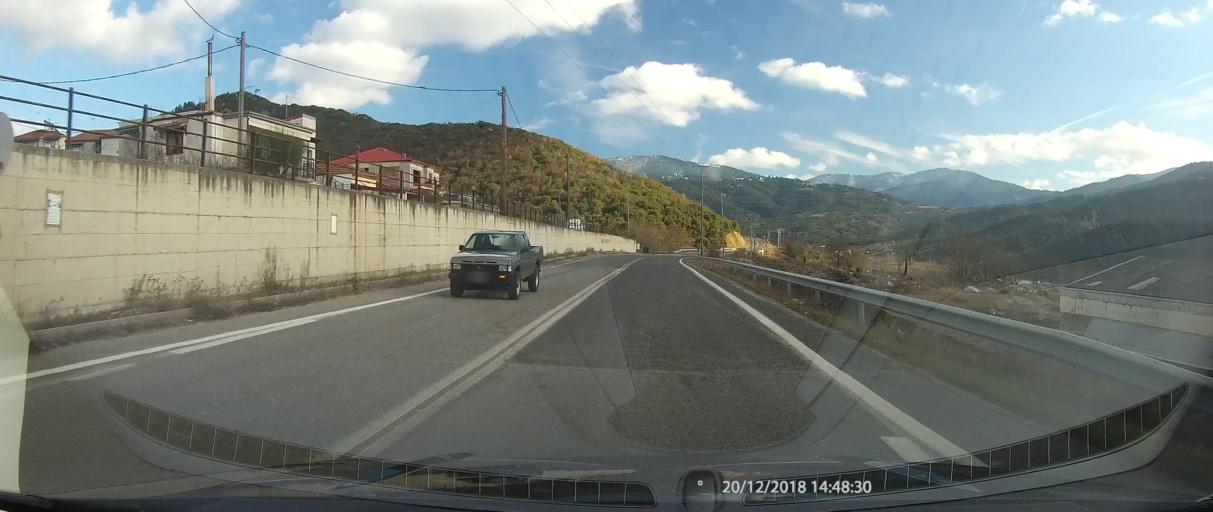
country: GR
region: Central Greece
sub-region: Nomos Evrytanias
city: Karpenisi
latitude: 38.9047
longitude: 21.7903
